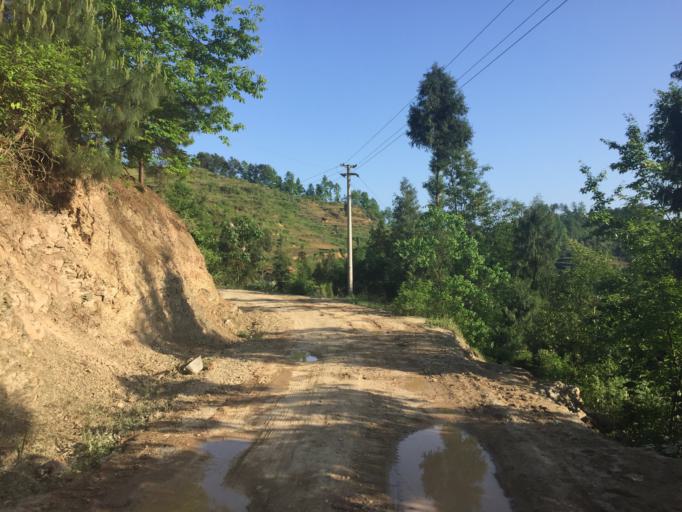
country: CN
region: Guizhou Sheng
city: Xujiaba
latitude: 27.7161
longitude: 108.0251
